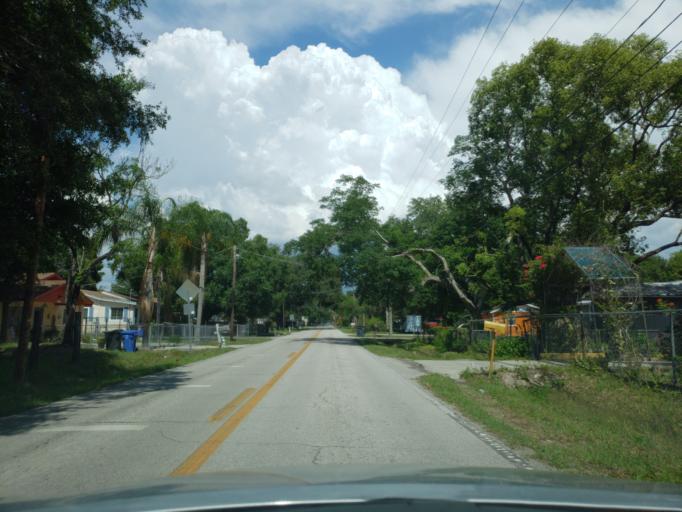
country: US
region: Florida
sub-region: Hillsborough County
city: Palm River-Clair Mel
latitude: 27.9336
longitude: -82.3910
